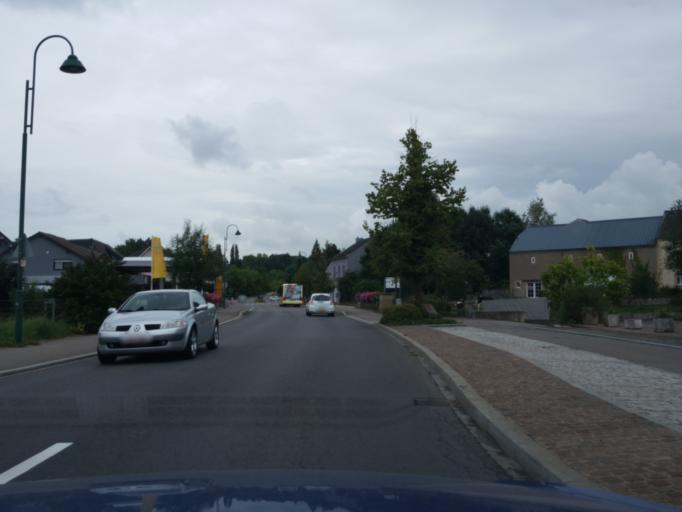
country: LU
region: Luxembourg
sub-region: Canton de Capellen
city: Mamer
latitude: 49.6267
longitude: 6.0332
